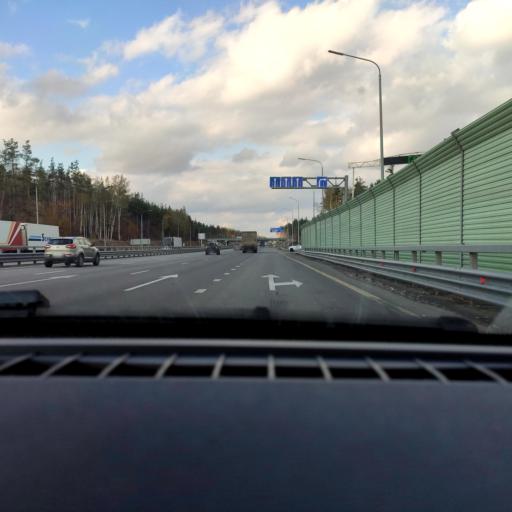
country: RU
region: Voronezj
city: Somovo
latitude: 51.6871
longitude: 39.3023
